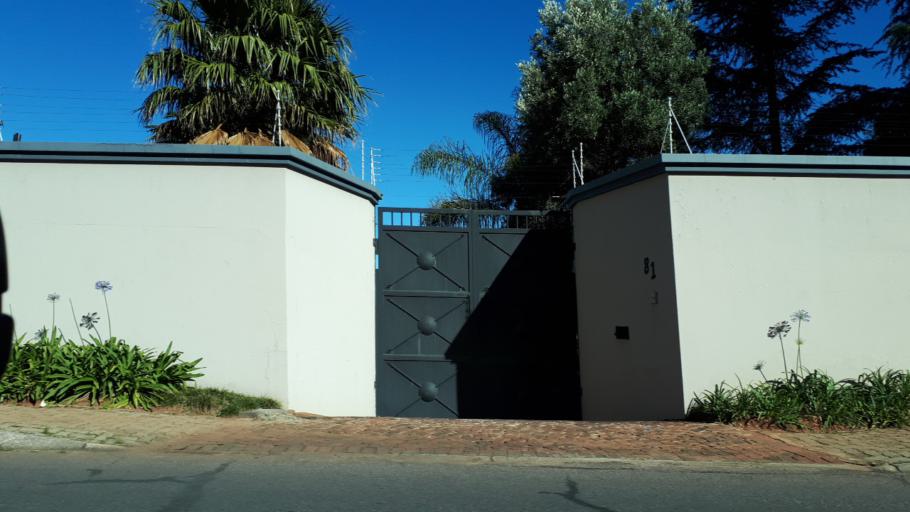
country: ZA
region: Gauteng
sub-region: Ekurhuleni Metropolitan Municipality
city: Germiston
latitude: -26.1792
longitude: 28.1511
